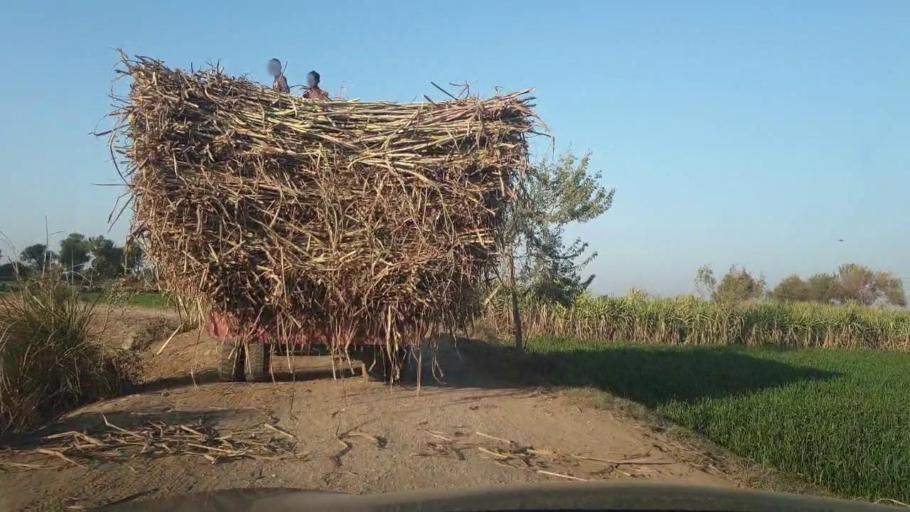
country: PK
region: Sindh
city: Mirpur Mathelo
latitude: 28.1521
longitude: 69.5649
